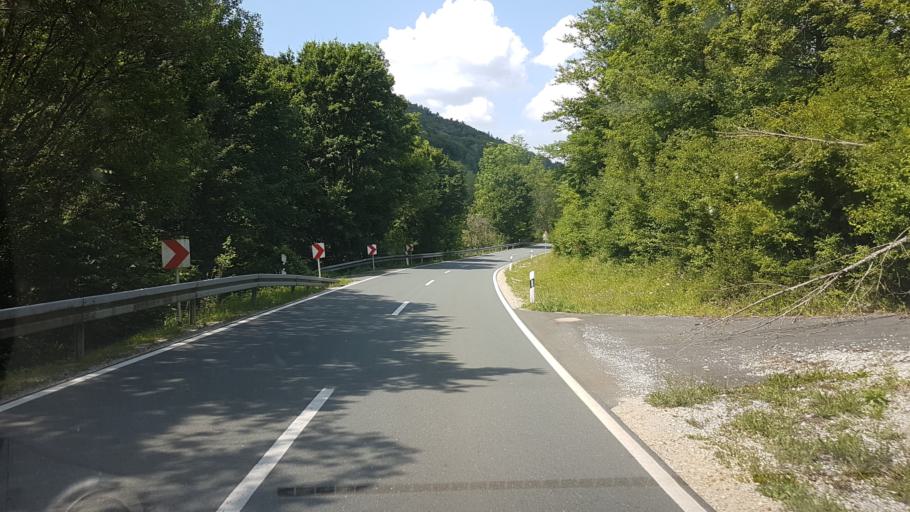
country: DE
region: Bavaria
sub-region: Upper Franconia
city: Egloffstein
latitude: 49.7448
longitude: 11.2426
